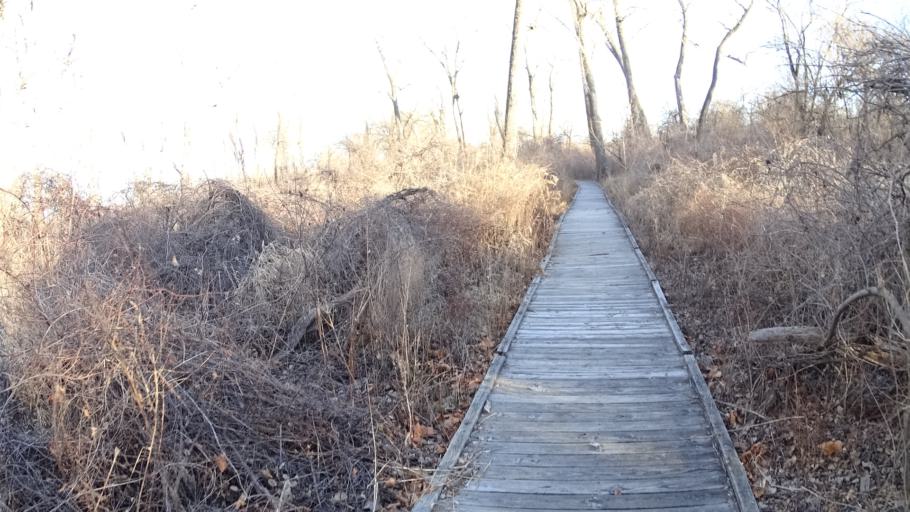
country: US
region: Nebraska
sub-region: Sarpy County
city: Bellevue
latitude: 41.1734
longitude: -95.8888
